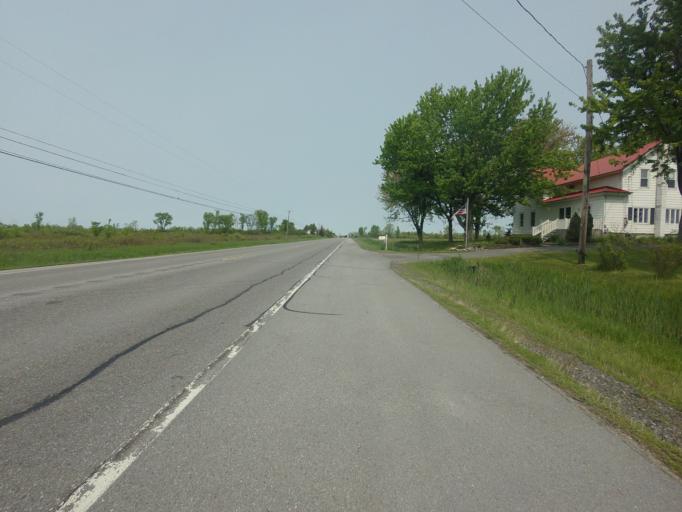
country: US
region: New York
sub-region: Jefferson County
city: Dexter
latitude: 44.0377
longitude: -76.0697
